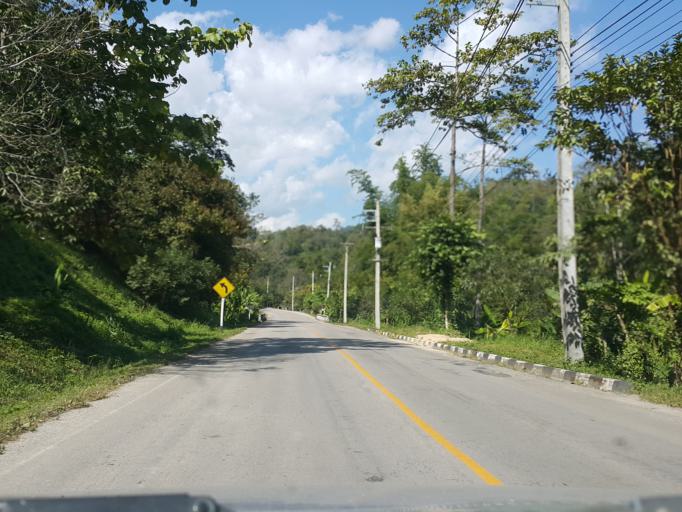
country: TH
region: Chiang Mai
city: Mae Taeng
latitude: 19.1973
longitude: 98.6833
